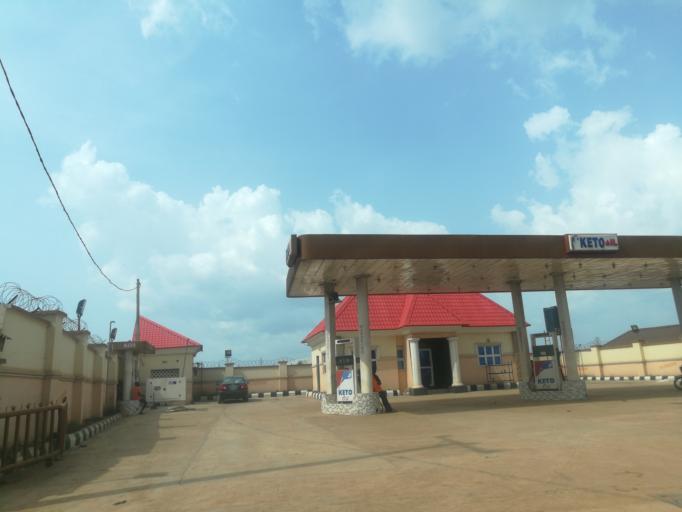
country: NG
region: Oyo
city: Moniya
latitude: 7.4709
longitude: 3.9171
